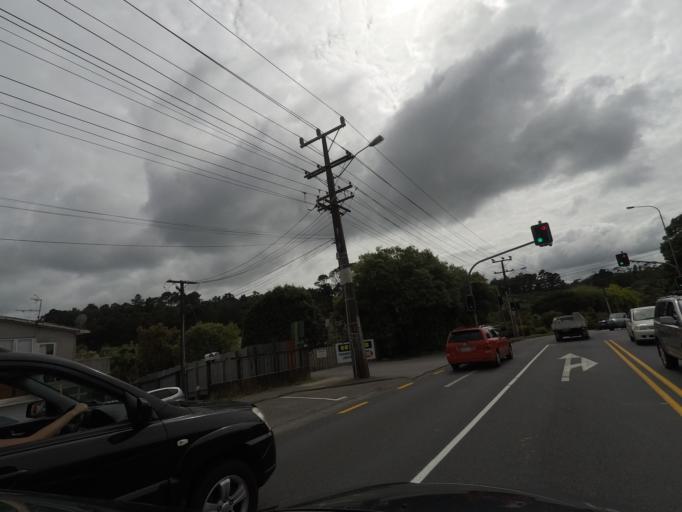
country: NZ
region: Auckland
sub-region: Auckland
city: Waitakere
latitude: -36.9085
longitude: 174.6411
